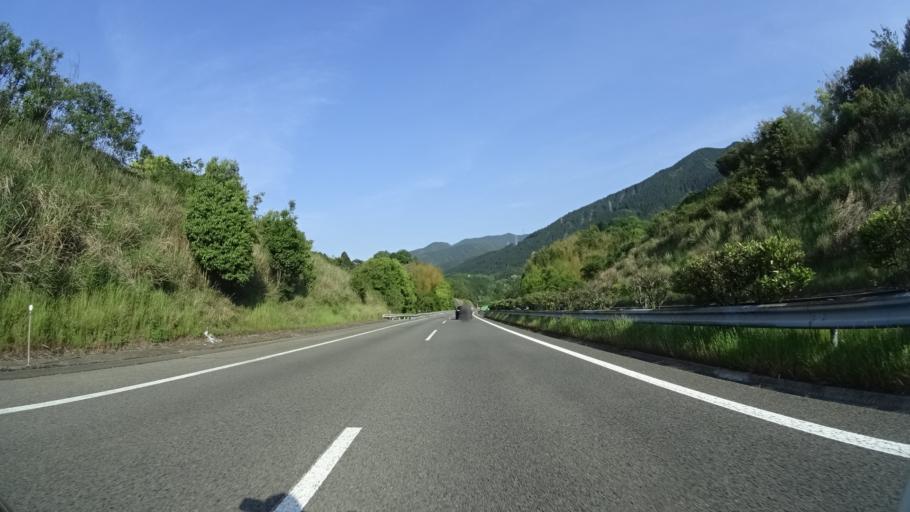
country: JP
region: Ehime
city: Saijo
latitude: 33.9114
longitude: 133.2455
